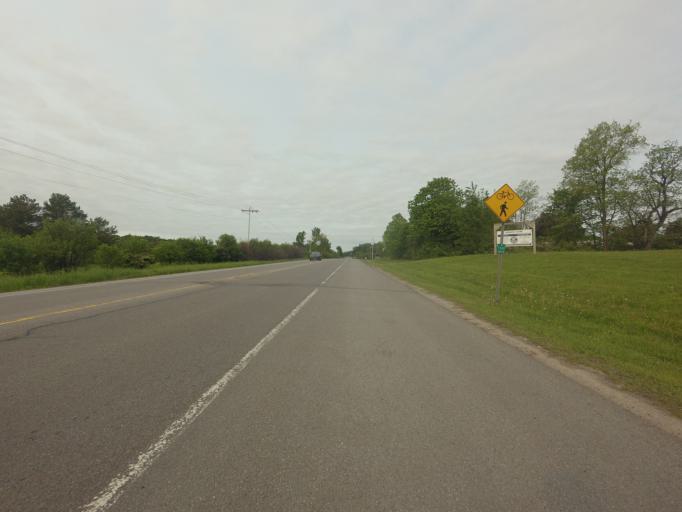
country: US
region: New York
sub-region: Jefferson County
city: Black River
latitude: 44.0053
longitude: -75.8014
